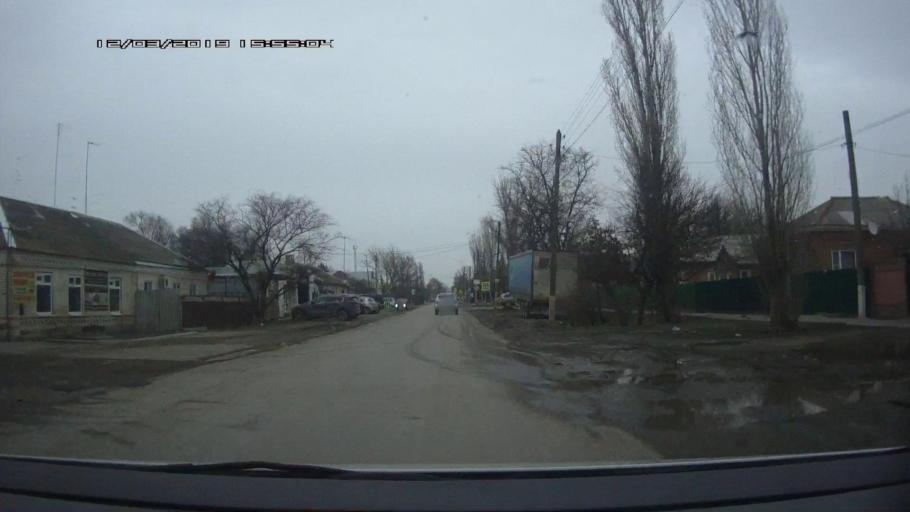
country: RU
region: Rostov
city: Novobataysk
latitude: 46.8944
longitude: 39.7790
